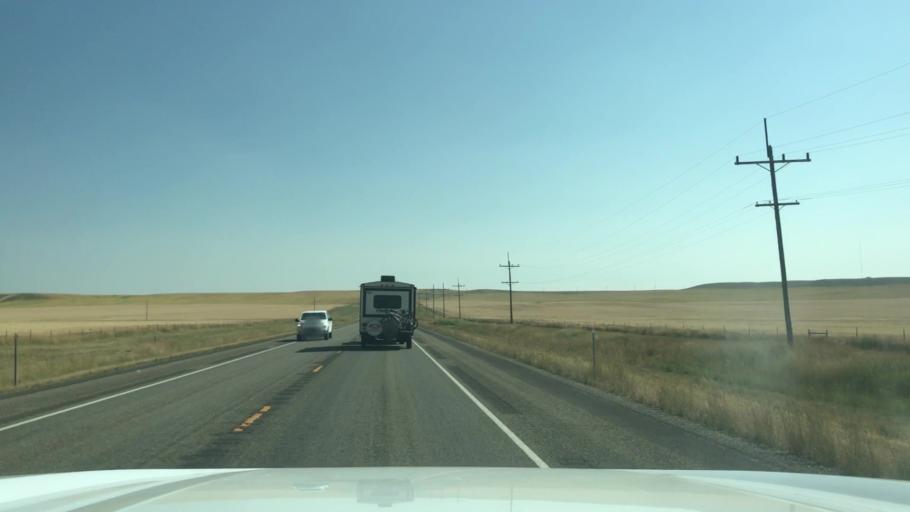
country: US
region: Montana
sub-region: Wheatland County
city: Harlowton
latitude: 46.4830
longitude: -109.7661
